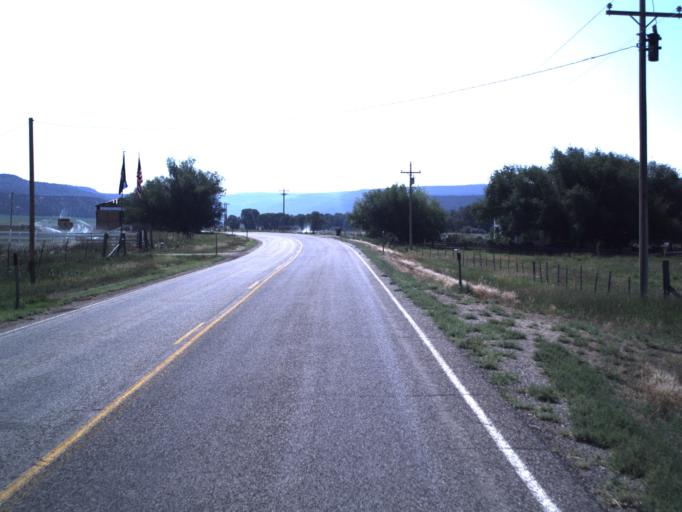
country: US
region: Utah
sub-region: Duchesne County
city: Duchesne
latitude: 40.3445
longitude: -110.6984
